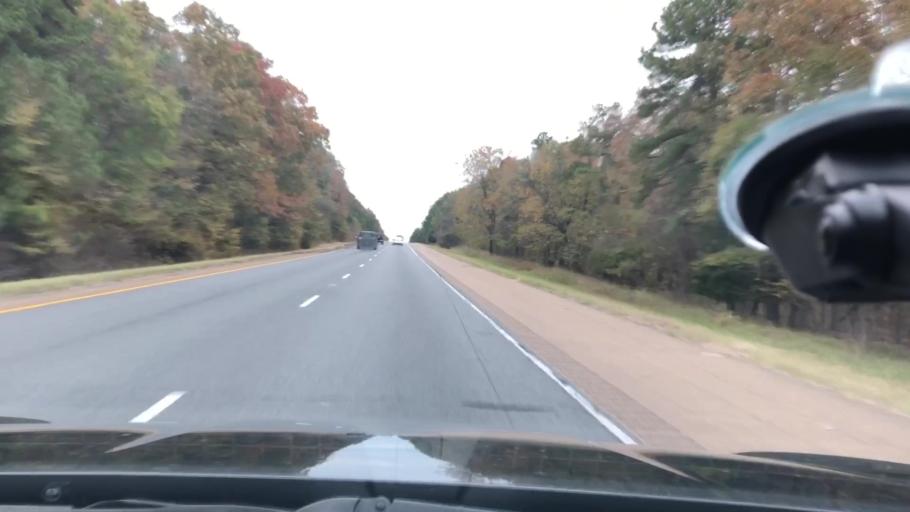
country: US
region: Arkansas
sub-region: Clark County
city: Gurdon
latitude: 33.9355
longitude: -93.2519
